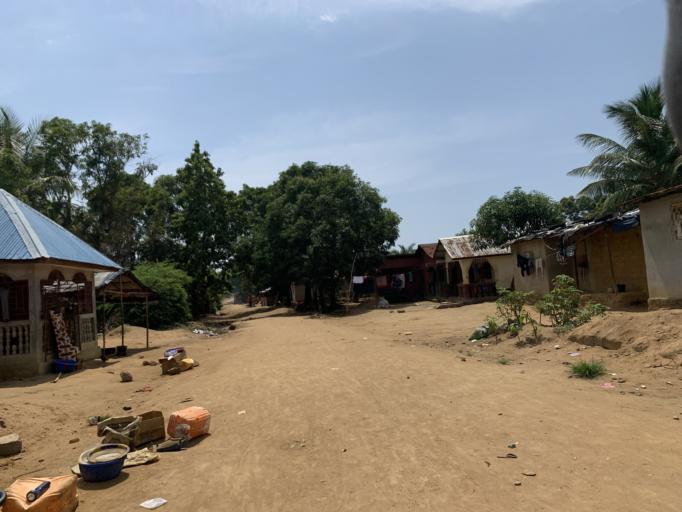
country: SL
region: Western Area
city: Waterloo
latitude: 8.3369
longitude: -13.0450
